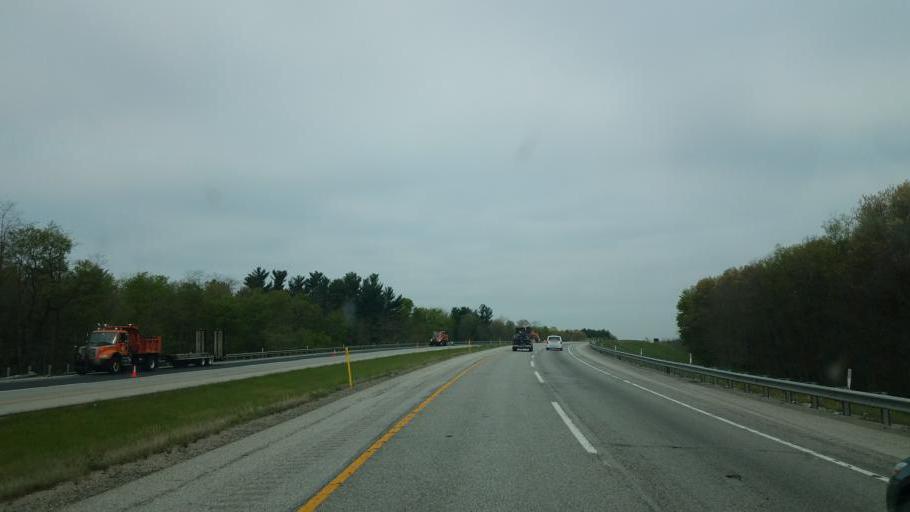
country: US
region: Indiana
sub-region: Elkhart County
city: Bristol
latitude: 41.7296
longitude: -85.7734
